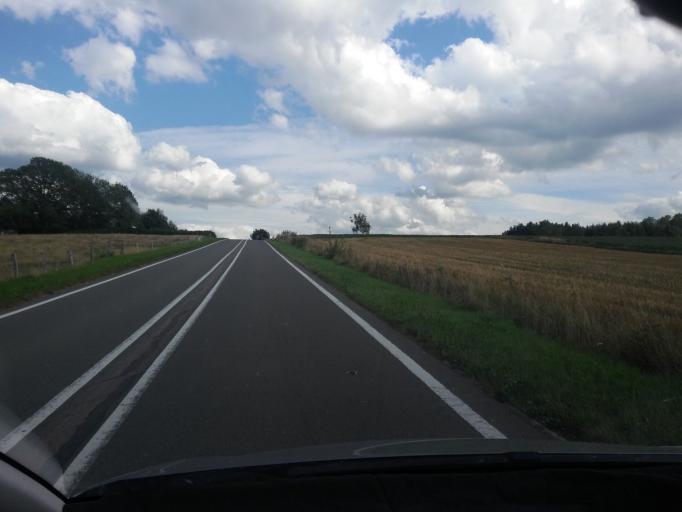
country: BE
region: Wallonia
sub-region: Province du Luxembourg
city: Saint-Hubert
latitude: 50.0303
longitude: 5.3343
